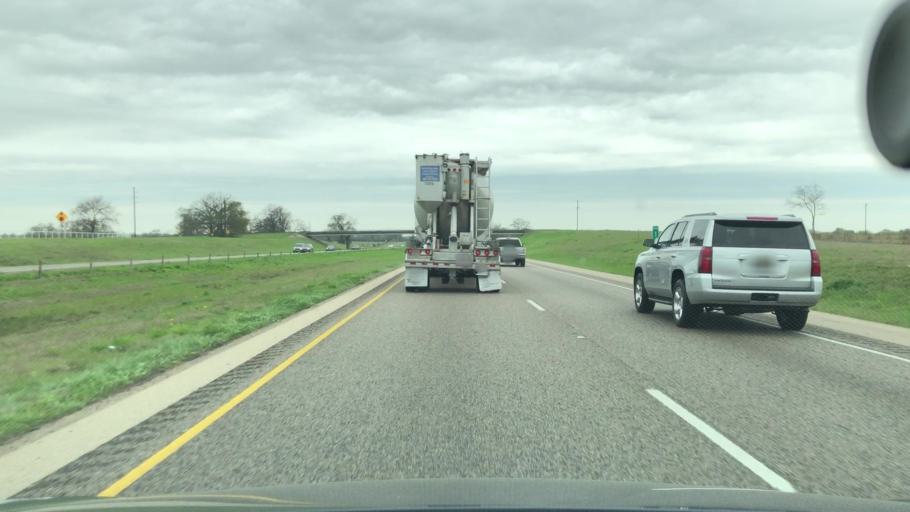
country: US
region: Texas
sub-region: Madison County
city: Madisonville
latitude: 31.0456
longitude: -95.9451
